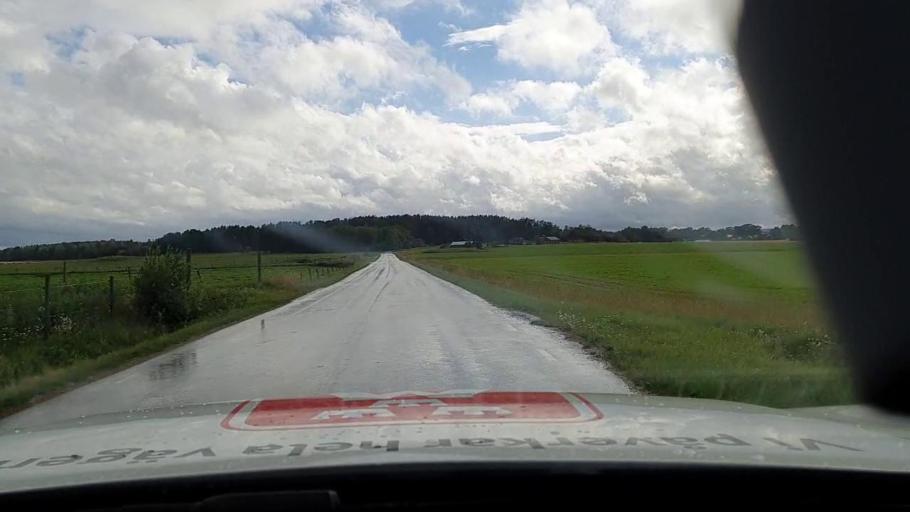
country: SE
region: Vaestra Goetaland
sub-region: Skovde Kommun
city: Stopen
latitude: 58.5324
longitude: 13.9483
